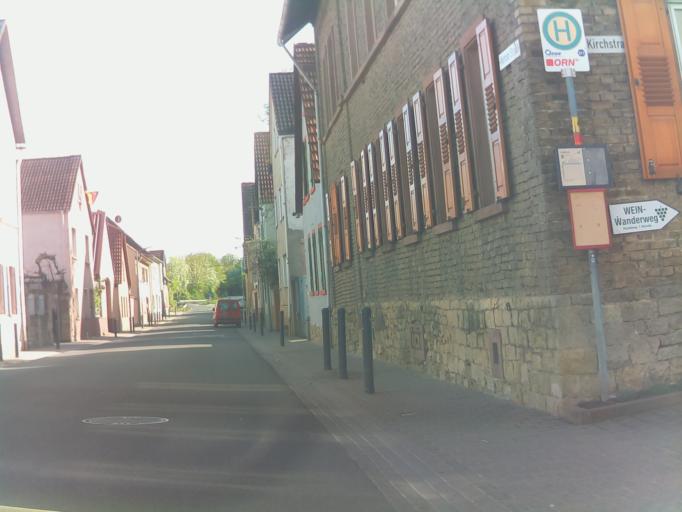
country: DE
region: Rheinland-Pfalz
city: Ludwigshohe
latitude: 49.8172
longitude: 8.3430
